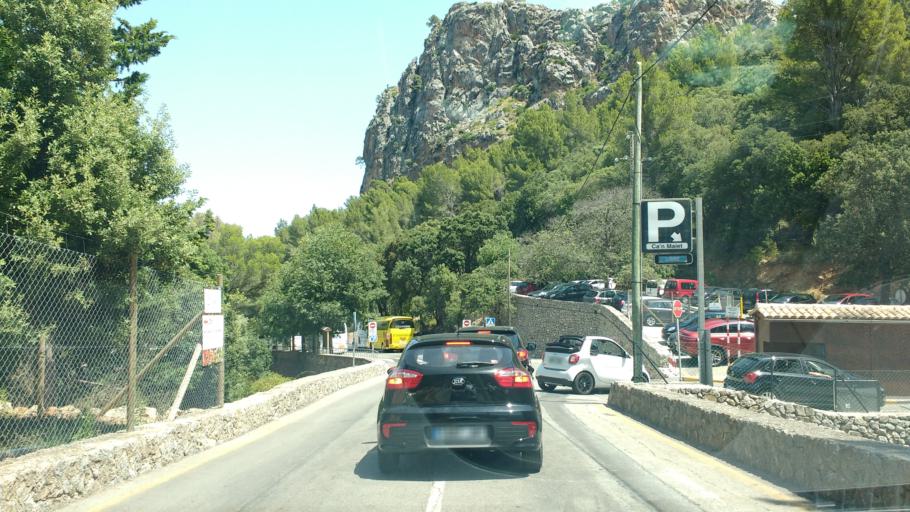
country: ES
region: Balearic Islands
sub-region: Illes Balears
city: Escorca
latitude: 39.8479
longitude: 2.7983
